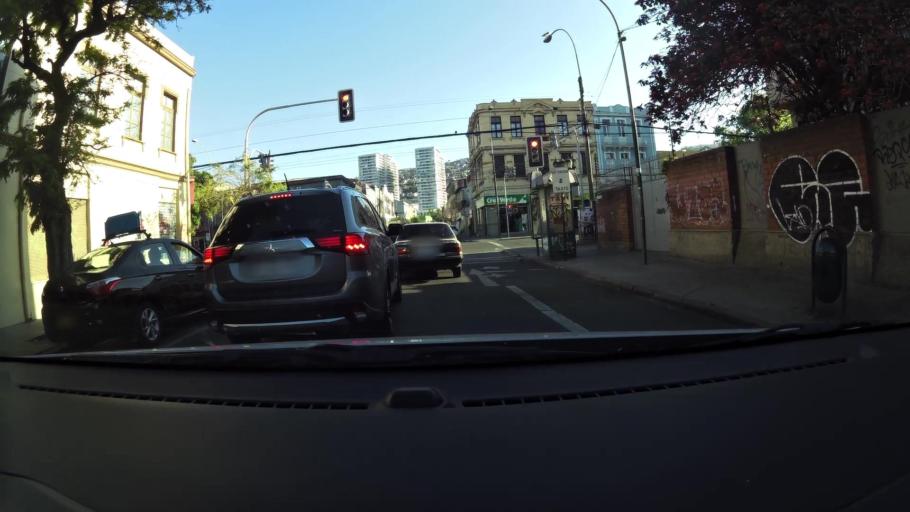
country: CL
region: Valparaiso
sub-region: Provincia de Valparaiso
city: Valparaiso
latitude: -33.0471
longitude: -71.6098
